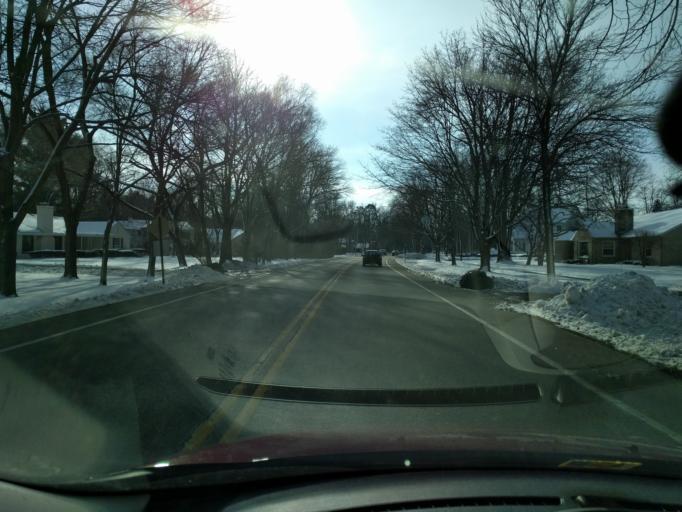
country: US
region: Wisconsin
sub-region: Milwaukee County
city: Fox Point
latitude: 43.1535
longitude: -87.8974
